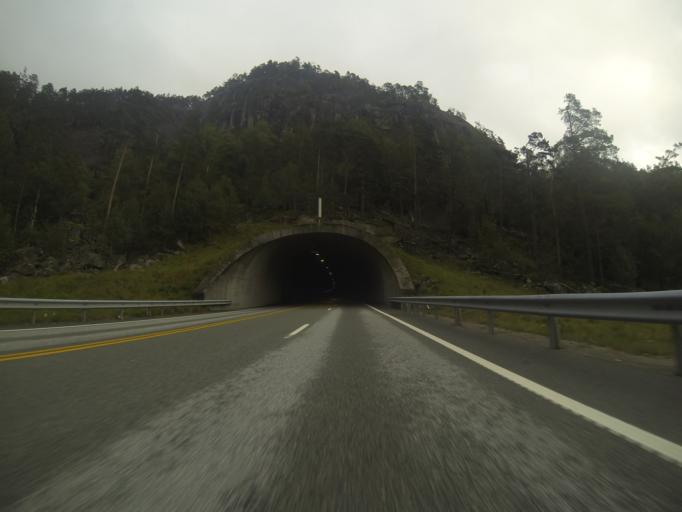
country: NO
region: Hordaland
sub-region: Odda
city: Odda
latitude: 59.8800
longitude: 6.4429
